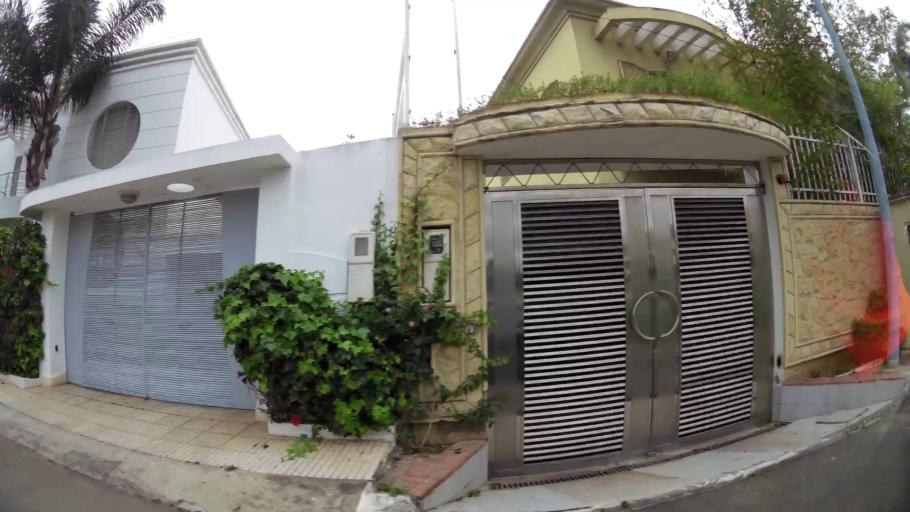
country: MA
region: Grand Casablanca
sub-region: Casablanca
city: Casablanca
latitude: 33.5469
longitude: -7.6385
